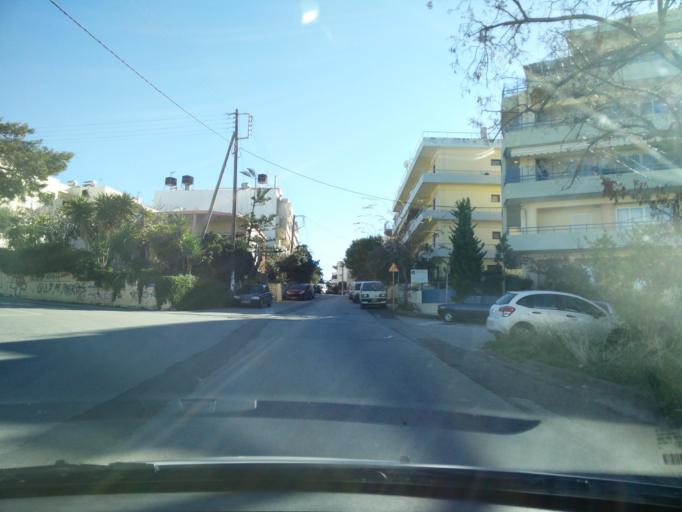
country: GR
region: Crete
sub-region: Nomos Irakleiou
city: Irakleion
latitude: 35.3296
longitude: 25.1413
